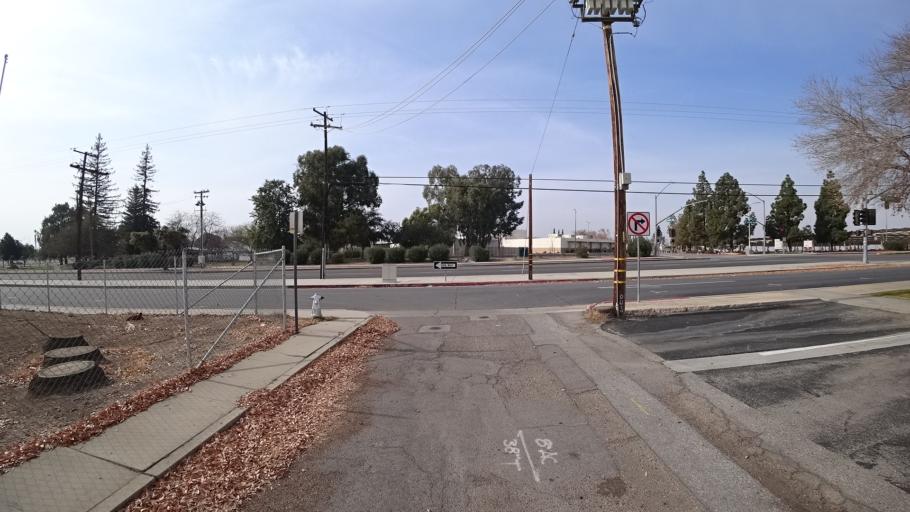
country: US
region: California
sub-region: Kern County
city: Oildale
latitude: 35.4102
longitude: -118.9672
